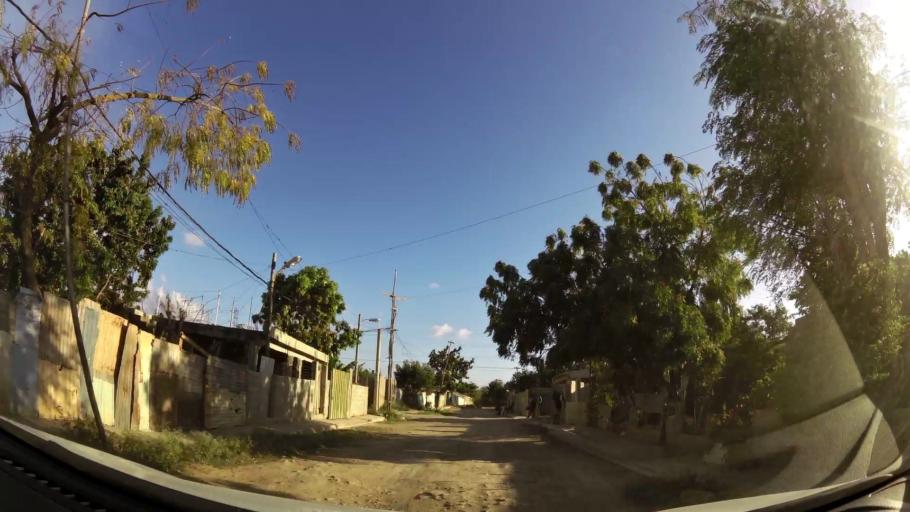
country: DO
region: Santo Domingo
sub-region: Santo Domingo
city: Santo Domingo Este
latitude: 18.4770
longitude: -69.7995
